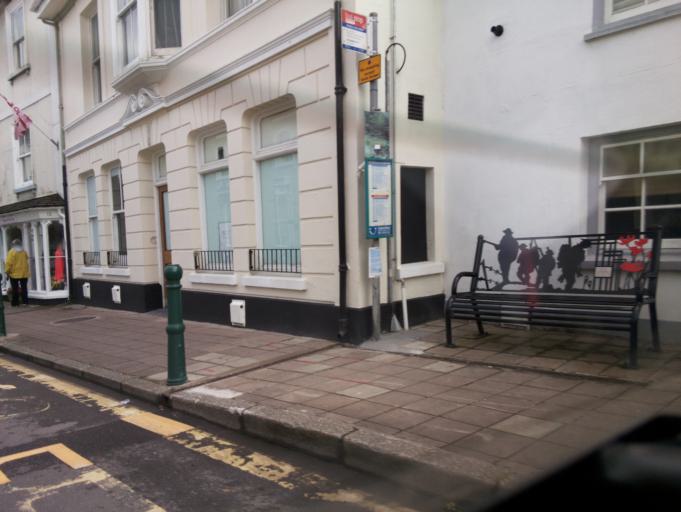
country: GB
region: England
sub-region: Devon
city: Modbury
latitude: 50.3490
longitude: -3.8867
